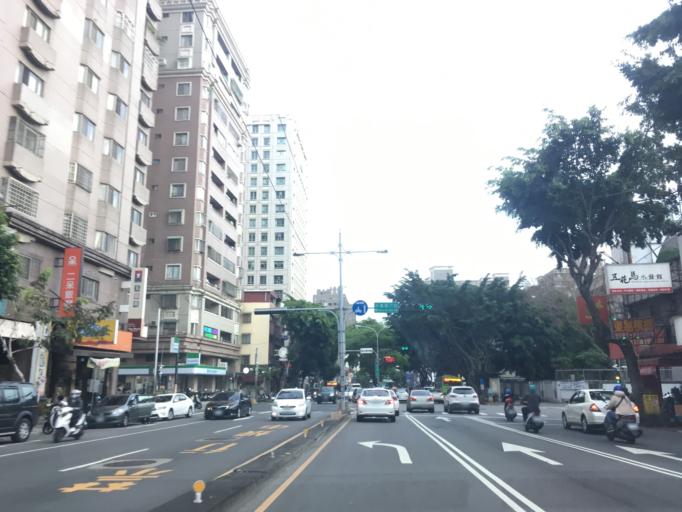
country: TW
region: Taiwan
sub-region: Taichung City
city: Taichung
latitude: 24.1763
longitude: 120.6857
